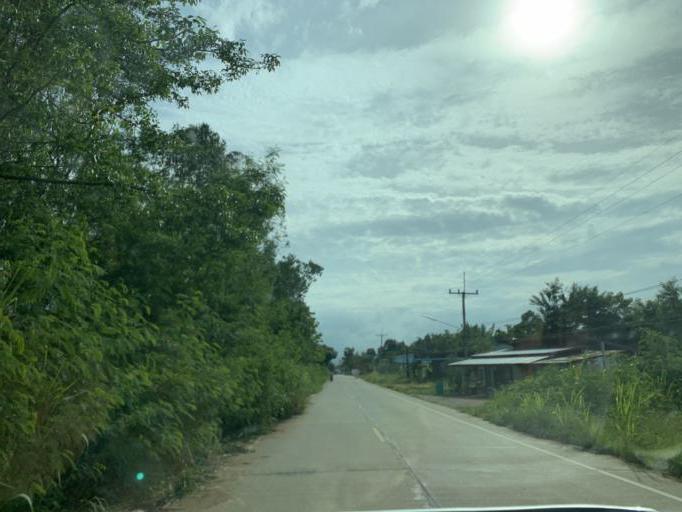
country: TH
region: Nakhon Sawan
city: Mae Wong
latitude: 15.8421
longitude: 99.4212
